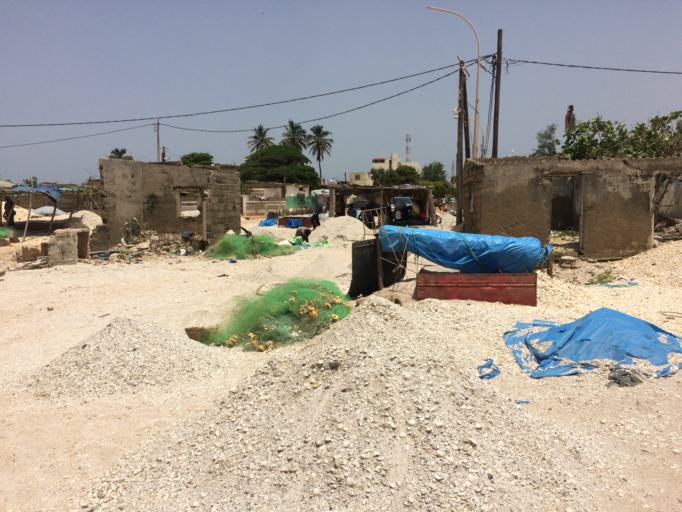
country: SN
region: Dakar
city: Pikine
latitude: 14.7325
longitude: -17.3339
